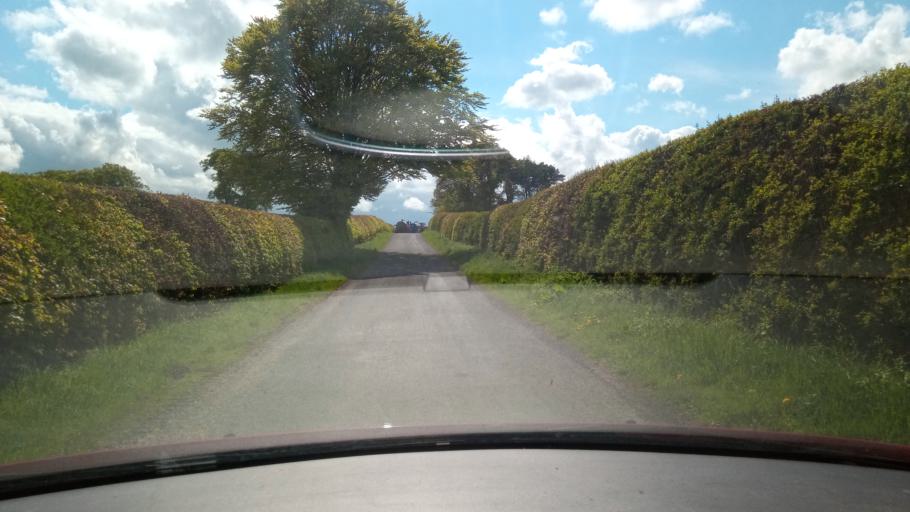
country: GB
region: Scotland
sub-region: The Scottish Borders
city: Saint Boswells
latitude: 55.5594
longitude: -2.6175
